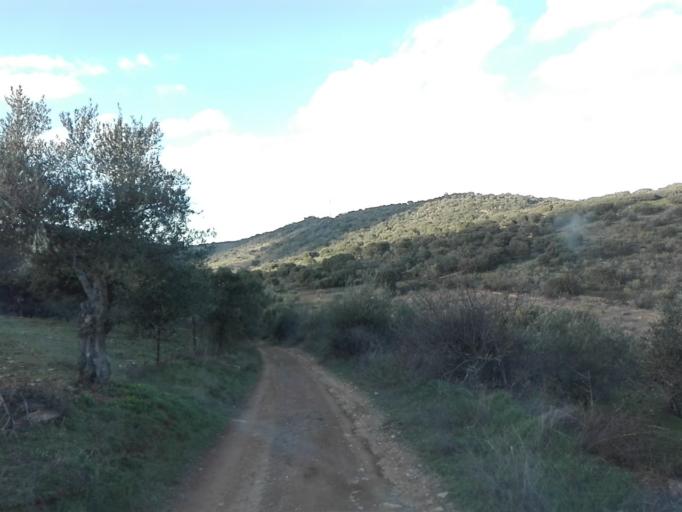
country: ES
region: Extremadura
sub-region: Provincia de Badajoz
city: Trasierra
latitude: 38.2060
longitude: -5.9994
